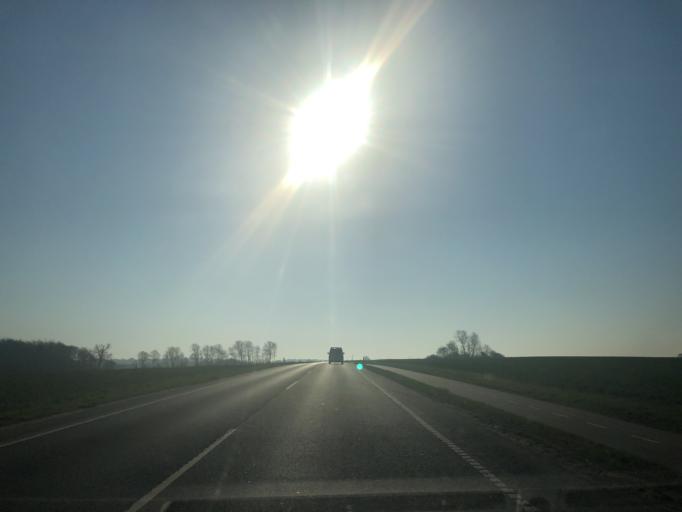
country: DK
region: Zealand
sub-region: Faxe Kommune
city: Fakse
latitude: 55.2553
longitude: 12.0782
